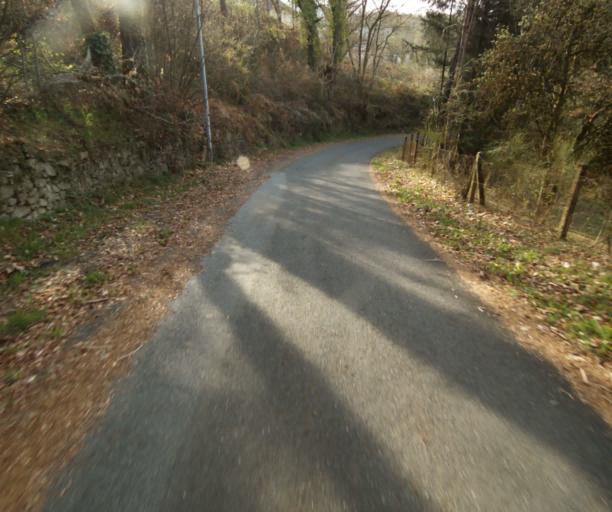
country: FR
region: Limousin
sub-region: Departement de la Correze
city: Correze
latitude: 45.3652
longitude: 1.8726
